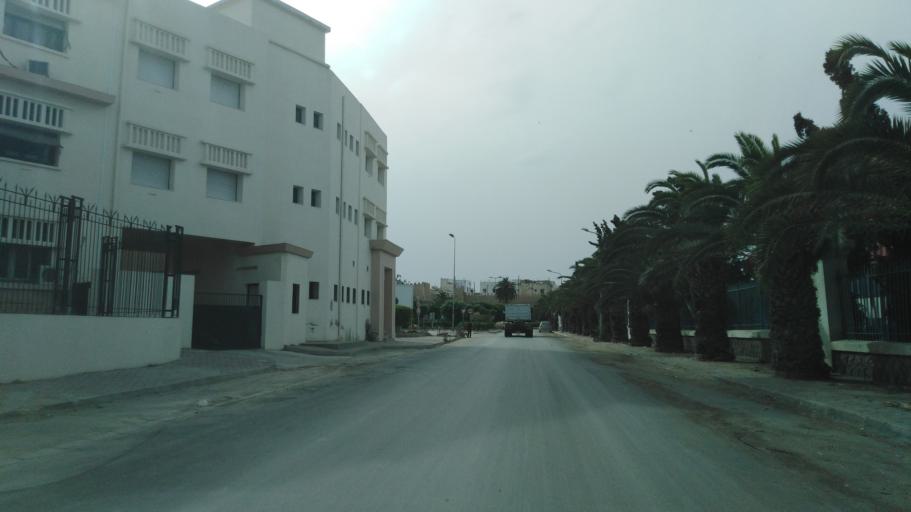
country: TN
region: Safaqis
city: Sfax
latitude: 34.7350
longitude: 10.7657
